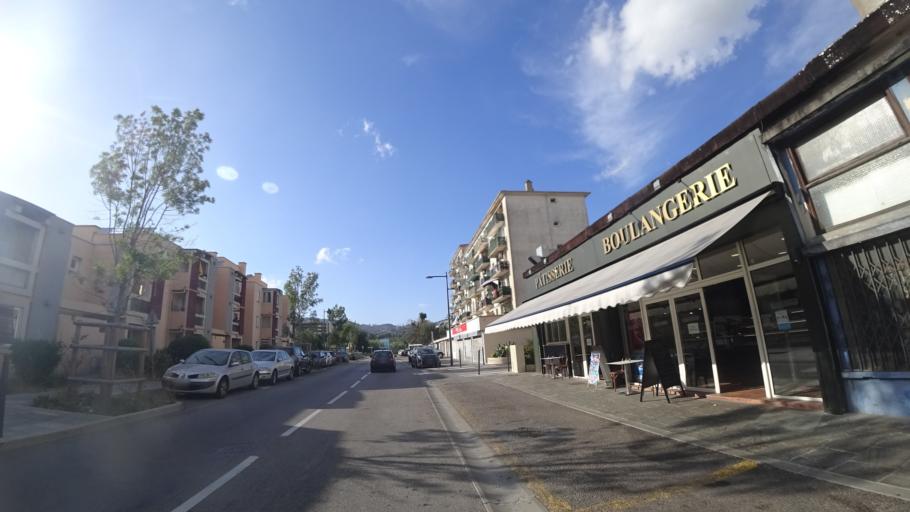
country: FR
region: Corsica
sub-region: Departement de la Corse-du-Sud
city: Ajaccio
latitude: 41.9355
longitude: 8.7433
